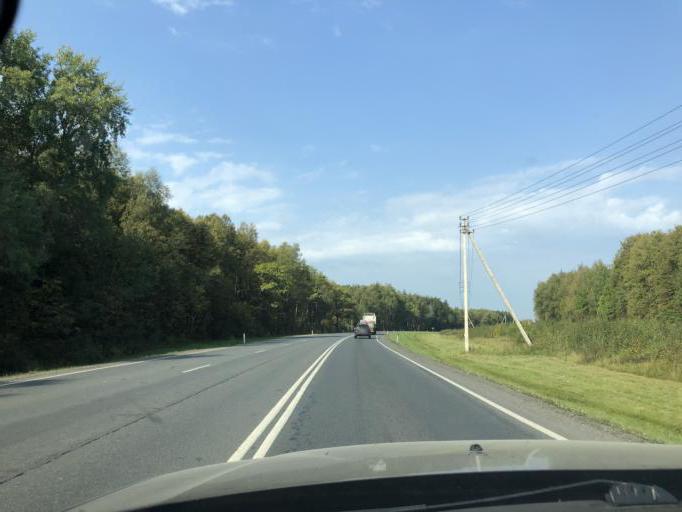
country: RU
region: Moskovskaya
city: L'vovskiy
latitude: 55.3347
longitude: 37.4750
